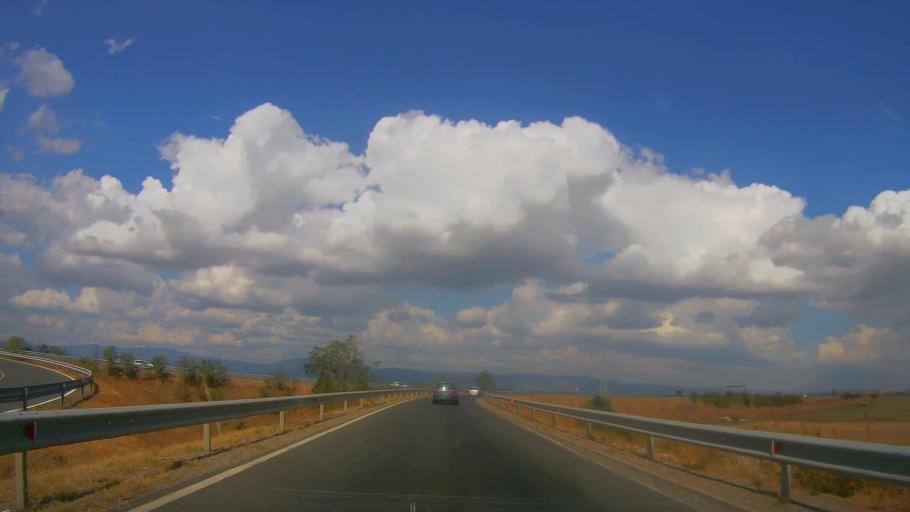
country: BG
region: Yambol
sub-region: Obshtina Yambol
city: Yambol
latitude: 42.5373
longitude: 26.4209
